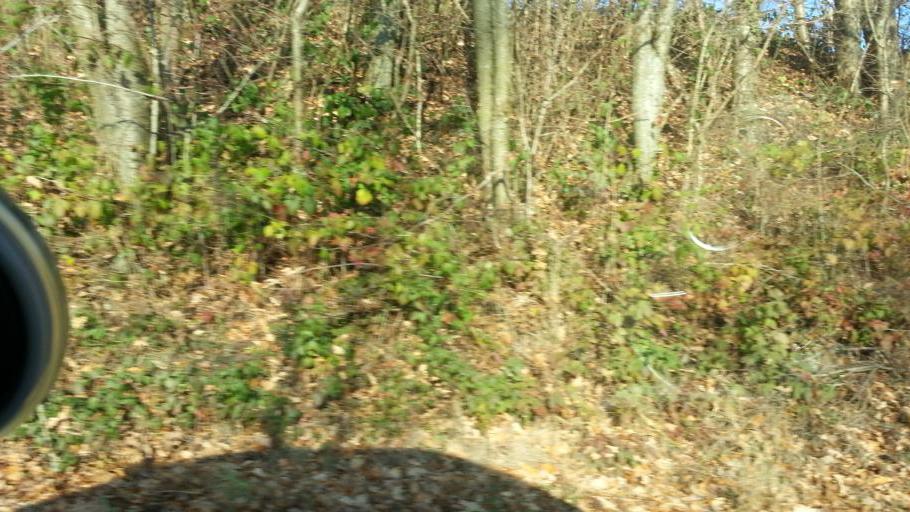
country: DE
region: Saarland
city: Tholey
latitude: 49.4840
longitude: 7.0417
